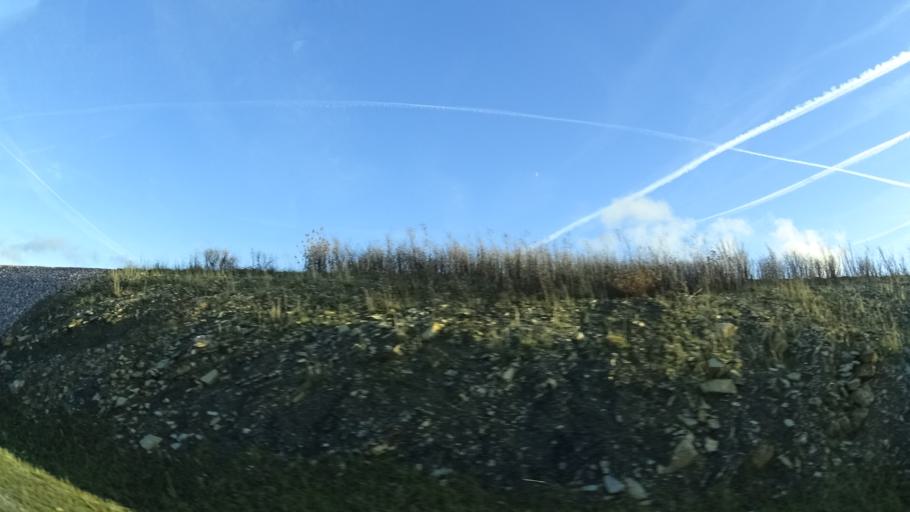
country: DE
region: Thuringia
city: Stadtilm
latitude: 50.7410
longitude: 11.0909
